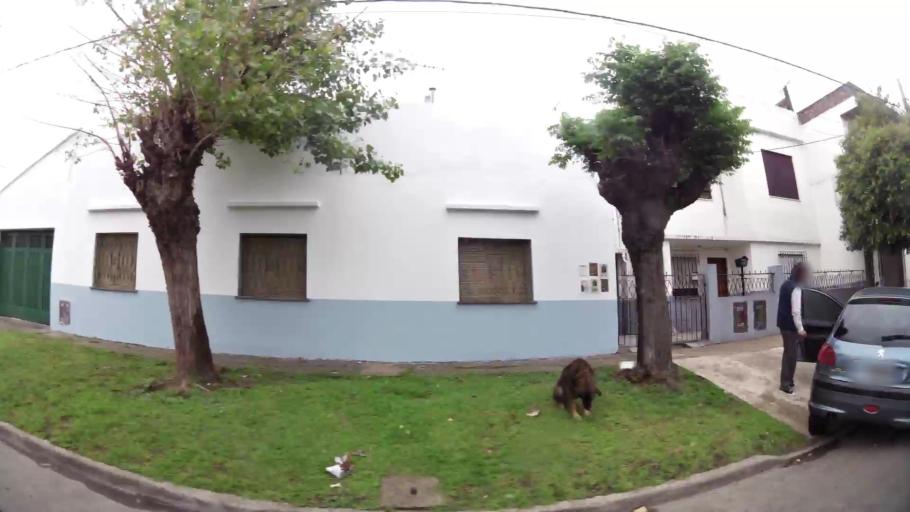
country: AR
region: Buenos Aires
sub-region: Partido de Lanus
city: Lanus
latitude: -34.7345
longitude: -58.3596
